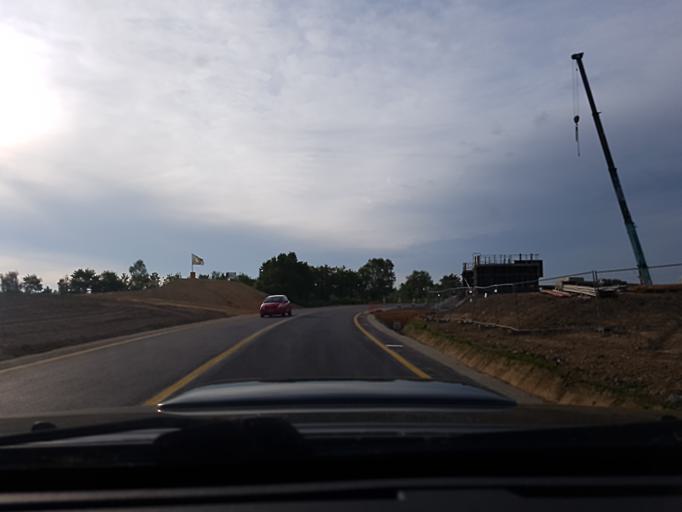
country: FR
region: Pays de la Loire
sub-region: Departement de la Vendee
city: Mache
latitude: 46.7643
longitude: -1.6544
